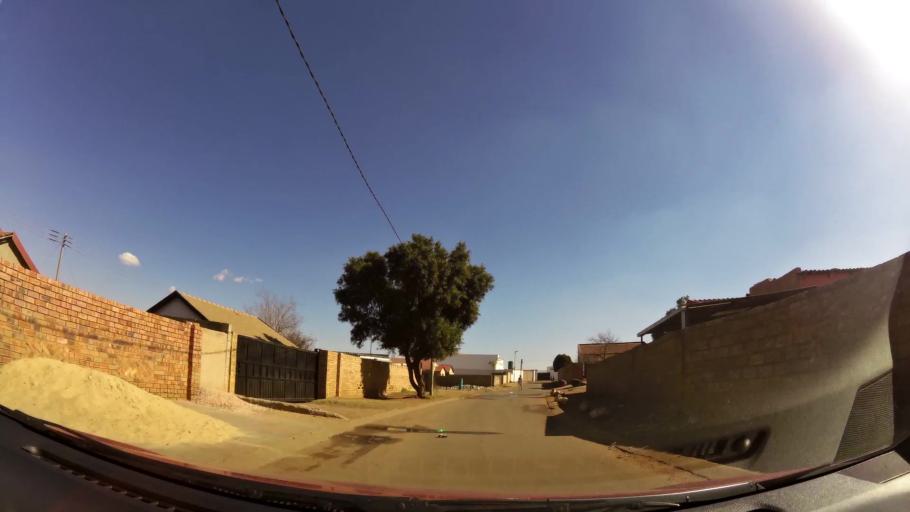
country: ZA
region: Gauteng
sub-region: City of Johannesburg Metropolitan Municipality
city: Soweto
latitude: -26.2513
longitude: 27.8066
